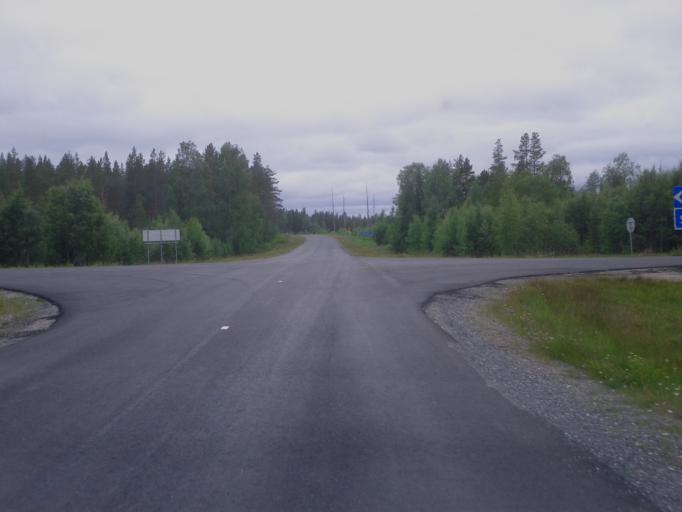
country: SE
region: Vaesterbotten
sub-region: Skelleftea Kommun
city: Storvik
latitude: 64.9873
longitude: 20.7106
